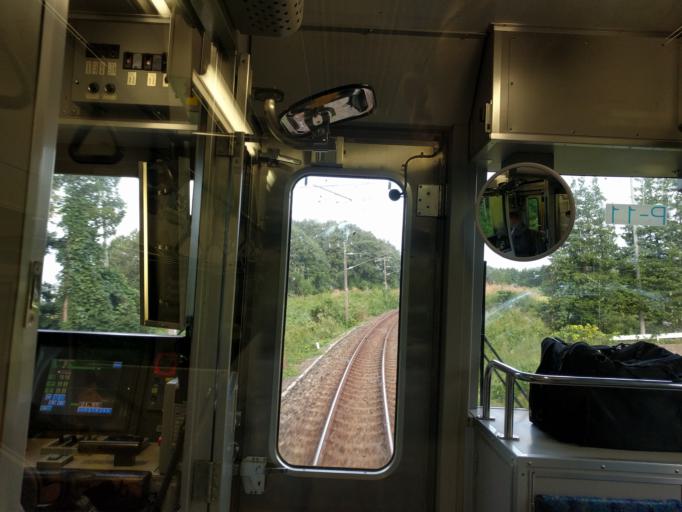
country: JP
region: Fukushima
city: Kitakata
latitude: 37.5597
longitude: 139.9687
